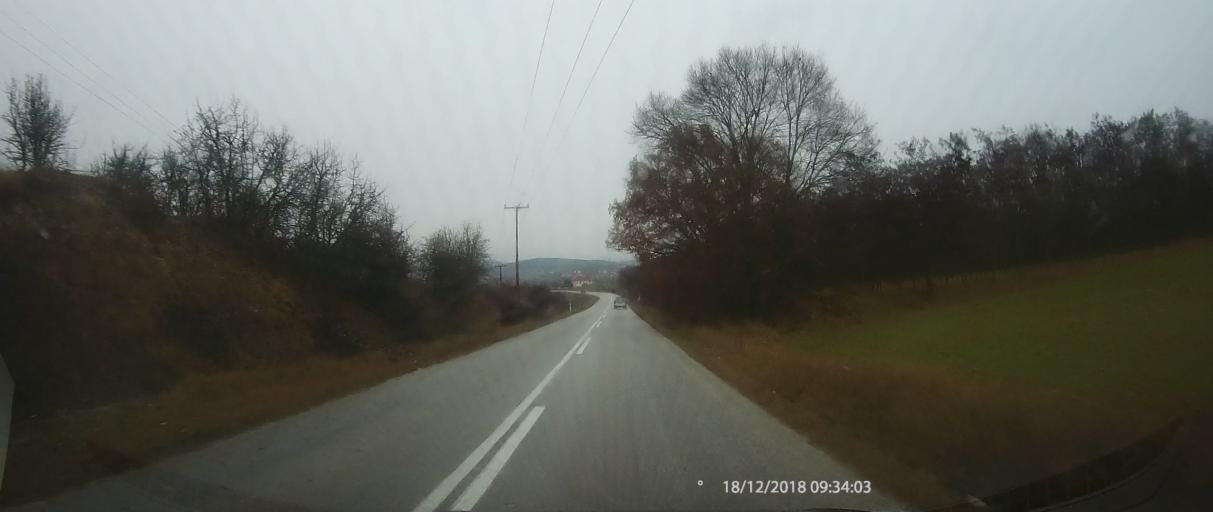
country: GR
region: Thessaly
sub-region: Nomos Larisis
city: Elassona
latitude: 39.9682
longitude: 22.1799
